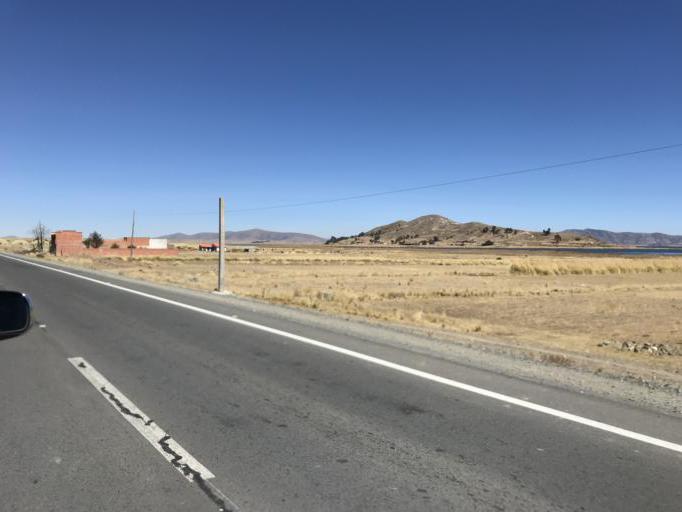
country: BO
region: La Paz
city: Huarina
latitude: -16.2149
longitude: -68.5898
